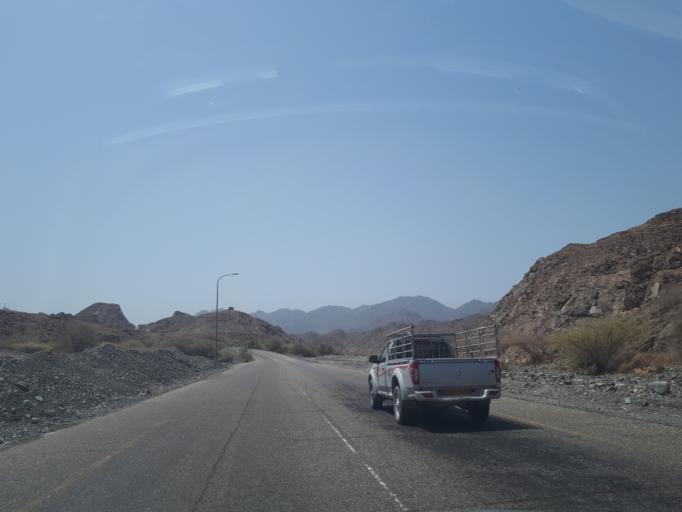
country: OM
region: Muhafazat ad Dakhiliyah
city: Sufalat Sama'il
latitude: 23.2027
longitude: 58.0820
